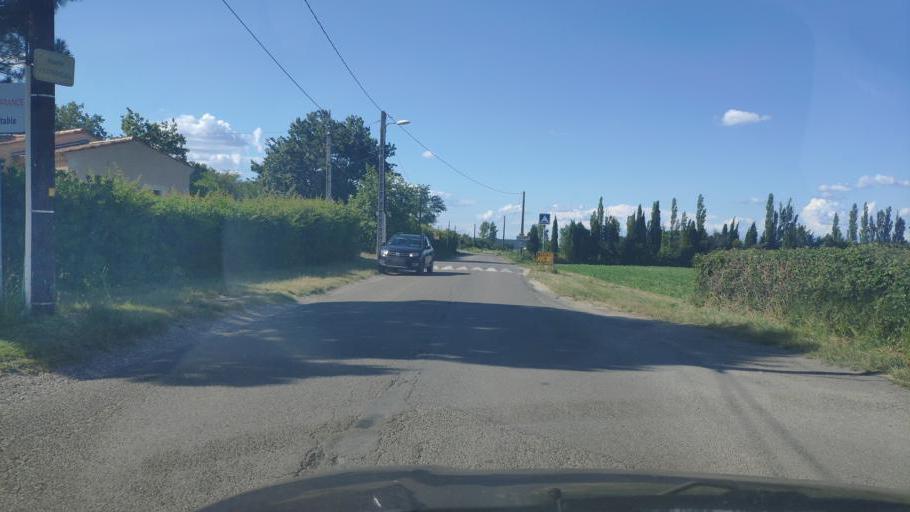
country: FR
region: Provence-Alpes-Cote d'Azur
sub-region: Departement du Vaucluse
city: Entraigues-sur-la-Sorgue
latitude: 43.9872
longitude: 4.9148
